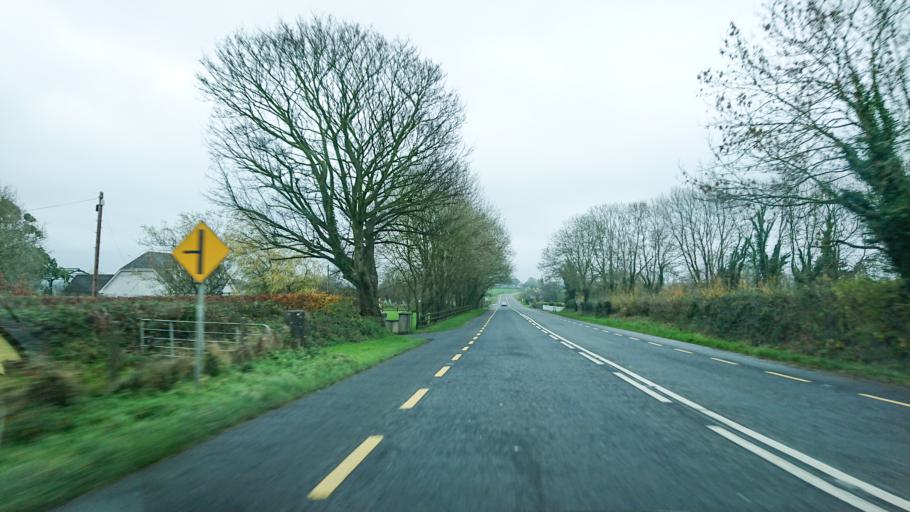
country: IE
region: Leinster
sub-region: Kilkenny
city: Mooncoin
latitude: 52.2862
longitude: -7.2175
